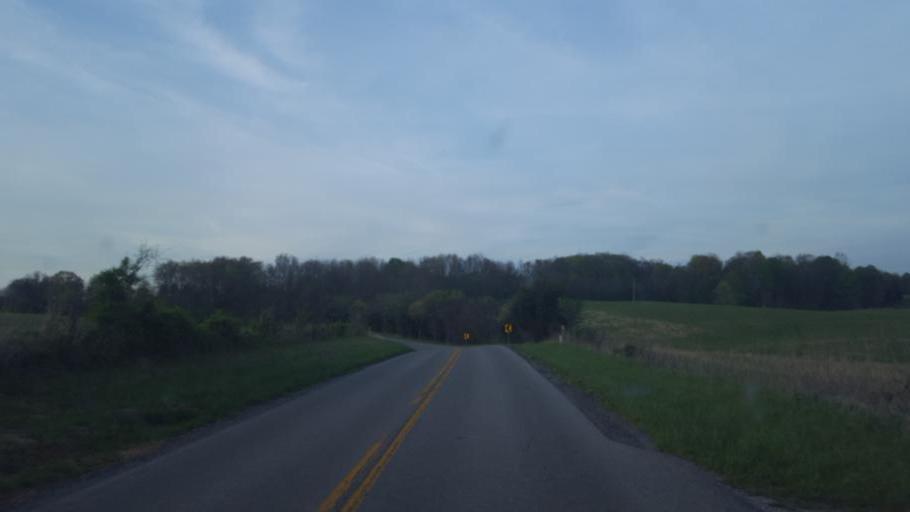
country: US
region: Kentucky
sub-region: Metcalfe County
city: Edmonton
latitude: 37.0870
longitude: -85.6977
